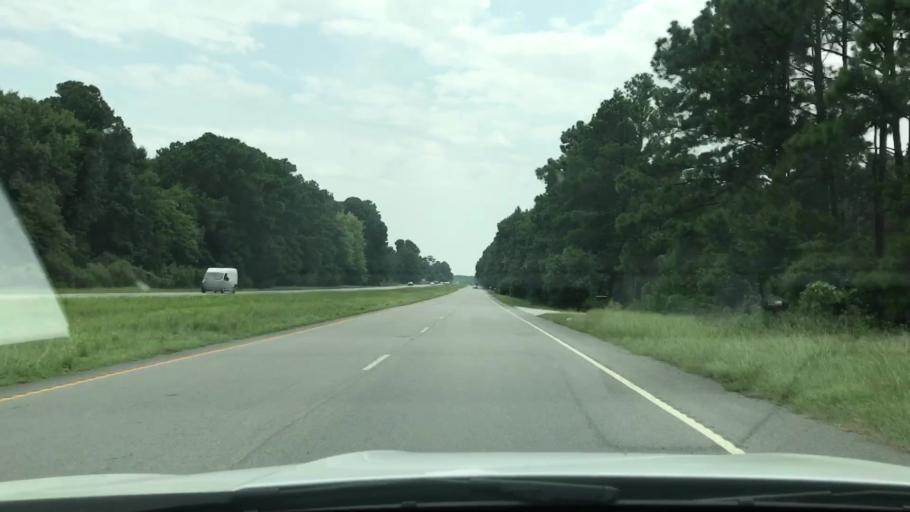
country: US
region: South Carolina
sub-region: Charleston County
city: Awendaw
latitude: 32.9354
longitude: -79.7124
